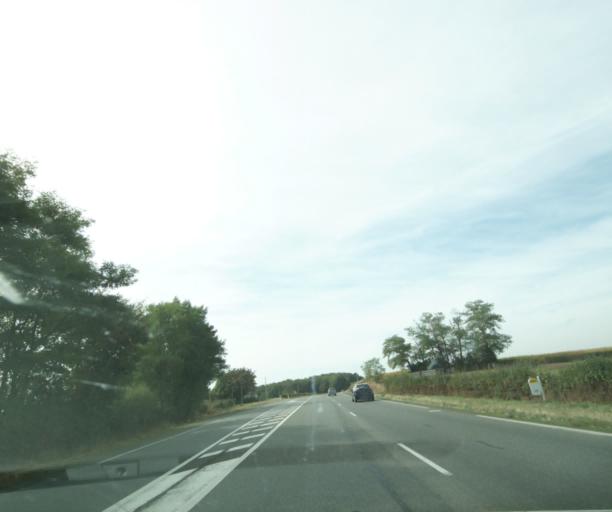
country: FR
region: Auvergne
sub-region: Departement de l'Allier
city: Lapalisse
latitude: 46.2407
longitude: 3.6097
